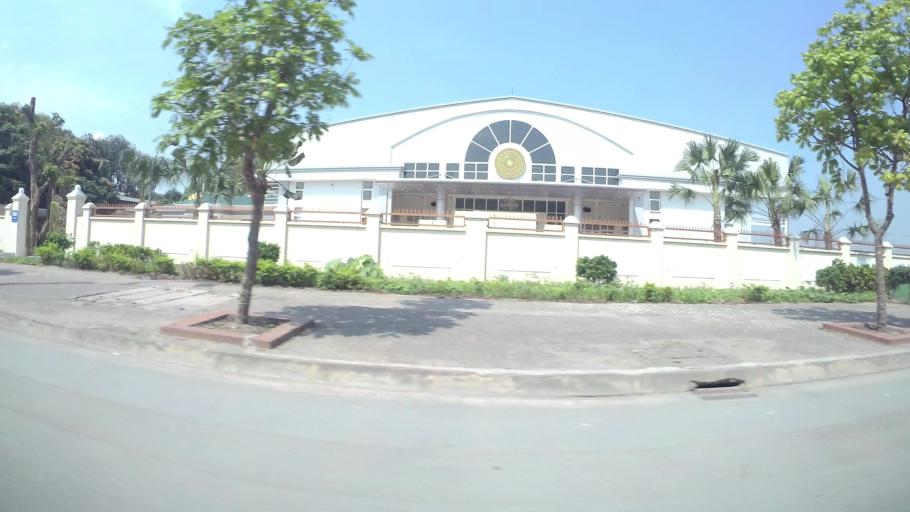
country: VN
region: Ha Noi
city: Hoan Kiem
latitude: 21.0679
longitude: 105.8799
